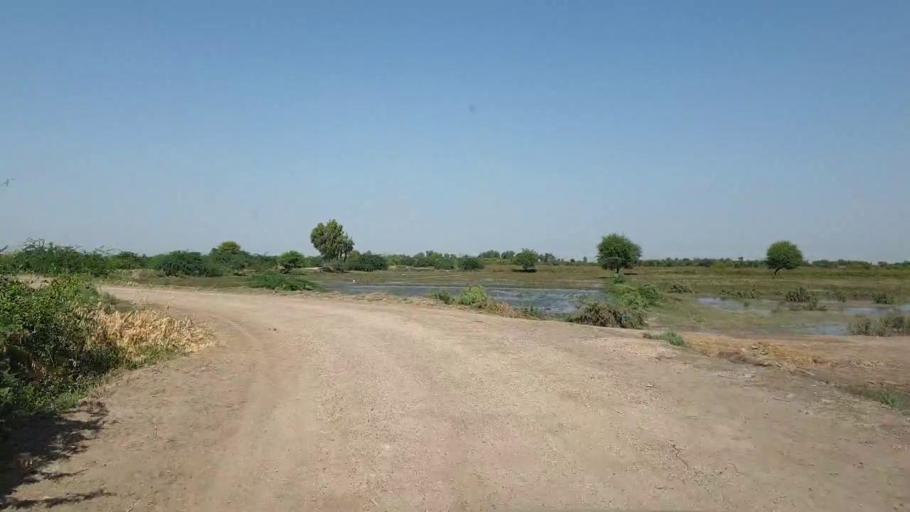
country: PK
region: Sindh
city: Tando Bago
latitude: 24.7356
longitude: 69.0431
